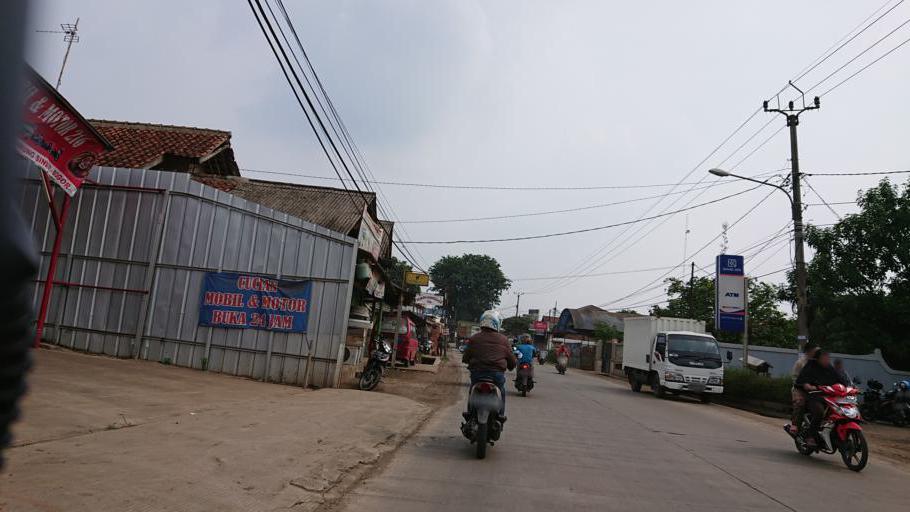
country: ID
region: West Java
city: Parung
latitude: -6.3831
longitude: 106.6803
